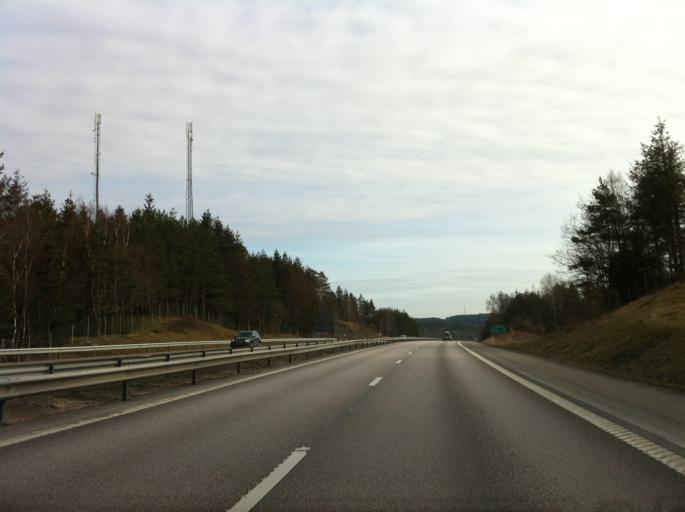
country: SE
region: Halland
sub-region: Kungsbacka Kommun
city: Kungsbacka
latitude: 57.5049
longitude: 12.0526
